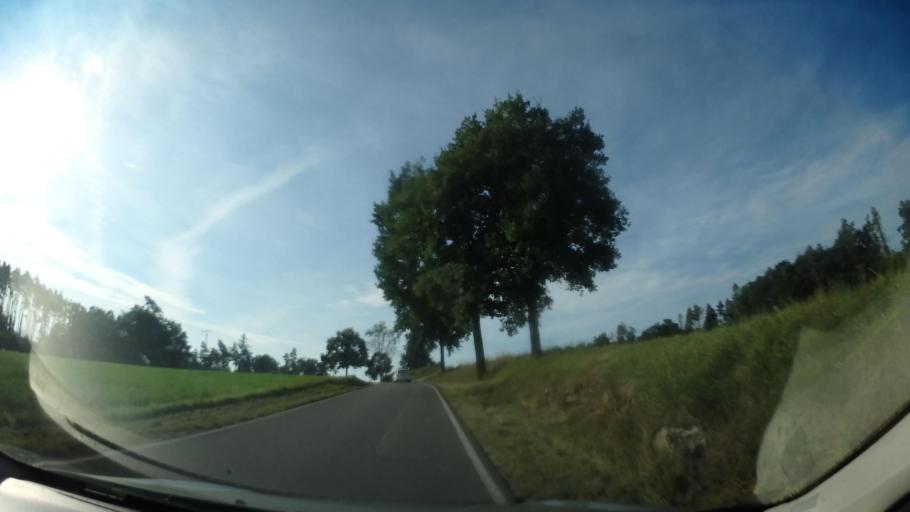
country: CZ
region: Jihocesky
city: Cimelice
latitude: 49.4364
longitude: 14.1260
